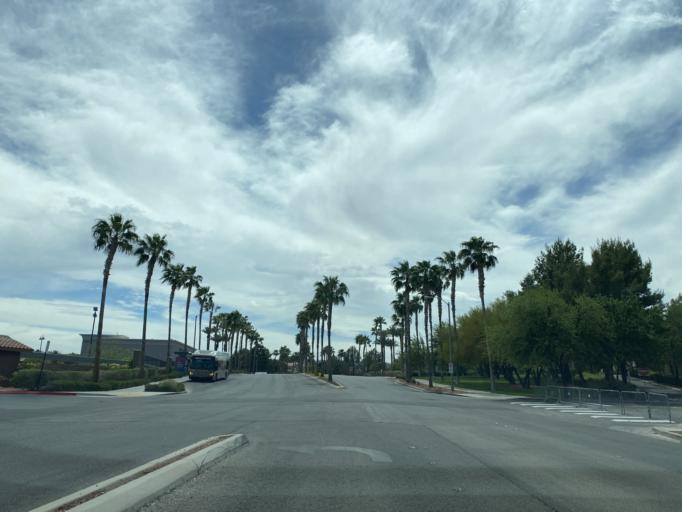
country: US
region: Nevada
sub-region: Clark County
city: Whitney
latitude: 36.0205
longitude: -115.0881
